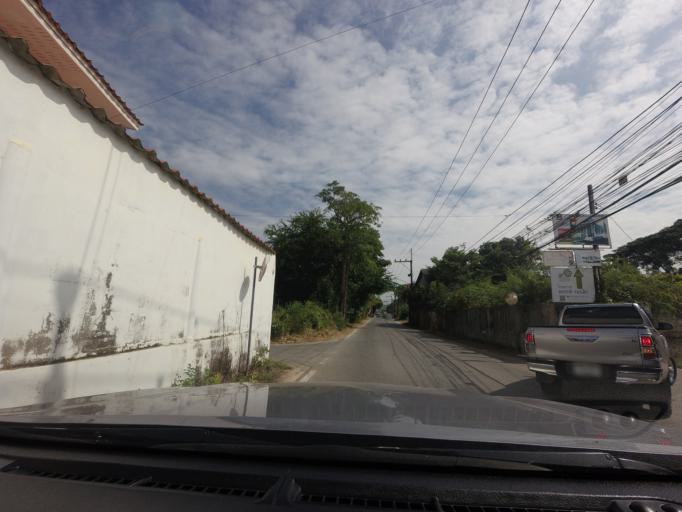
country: TH
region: Phitsanulok
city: Phitsanulok
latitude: 16.7971
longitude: 100.2474
